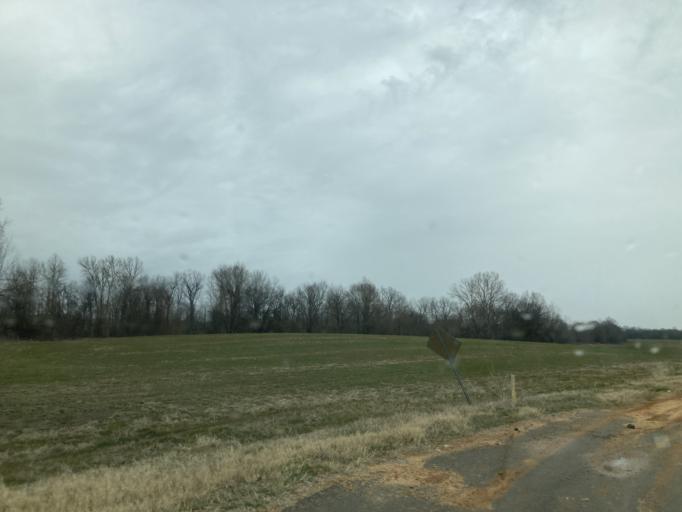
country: US
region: Mississippi
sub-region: Humphreys County
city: Belzoni
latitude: 33.0527
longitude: -90.4679
